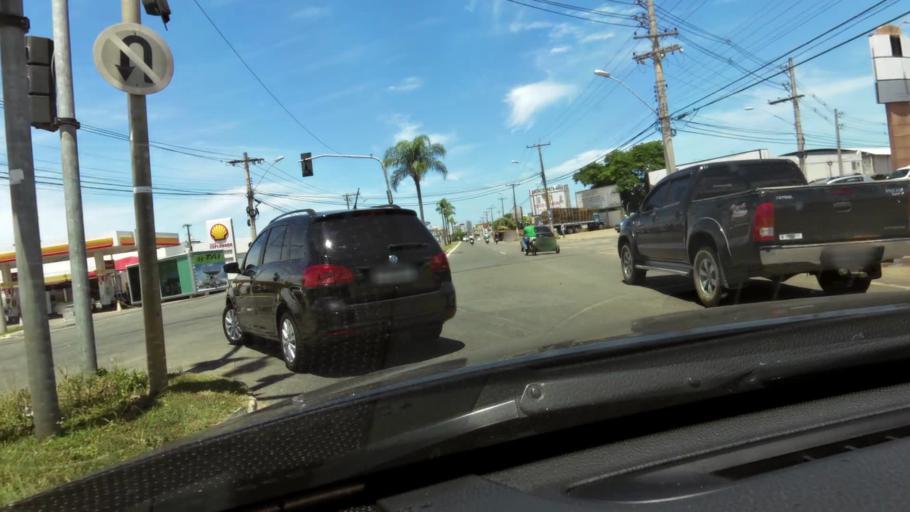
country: BR
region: Espirito Santo
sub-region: Vila Velha
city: Vila Velha
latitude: -20.3522
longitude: -40.2973
